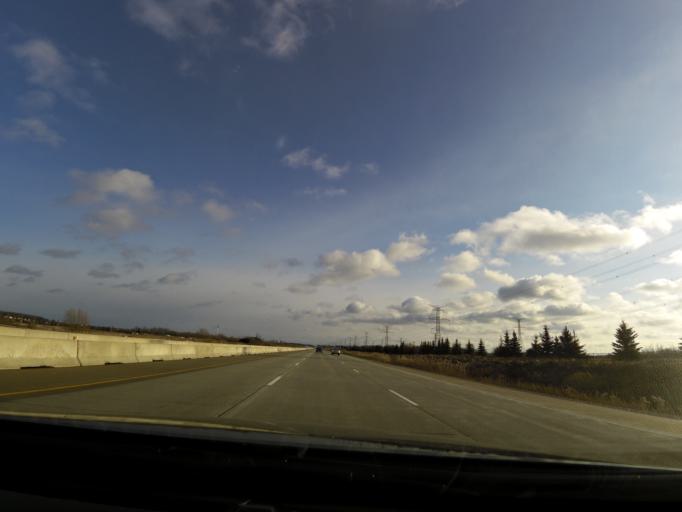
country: CA
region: Ontario
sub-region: Halton
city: Milton
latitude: 43.5645
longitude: -79.7809
